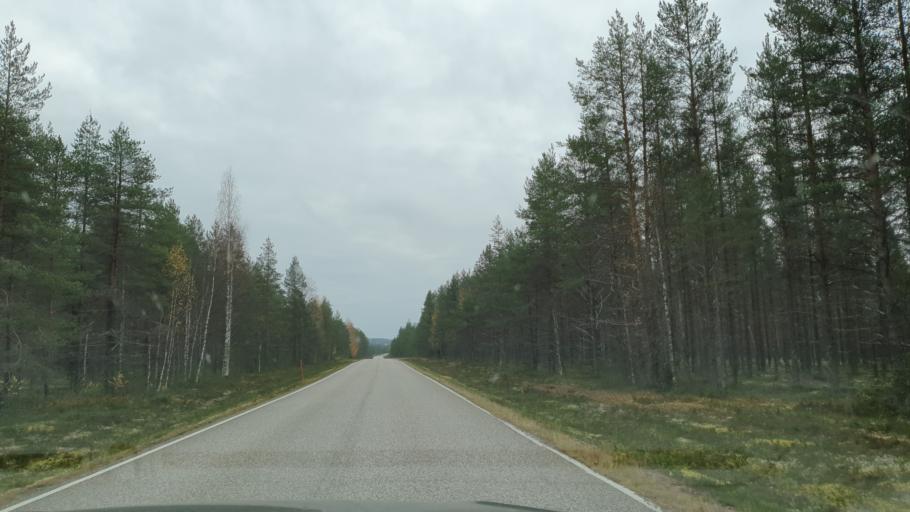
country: FI
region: Kainuu
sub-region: Kajaani
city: Paltamo
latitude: 64.6436
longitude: 27.9687
